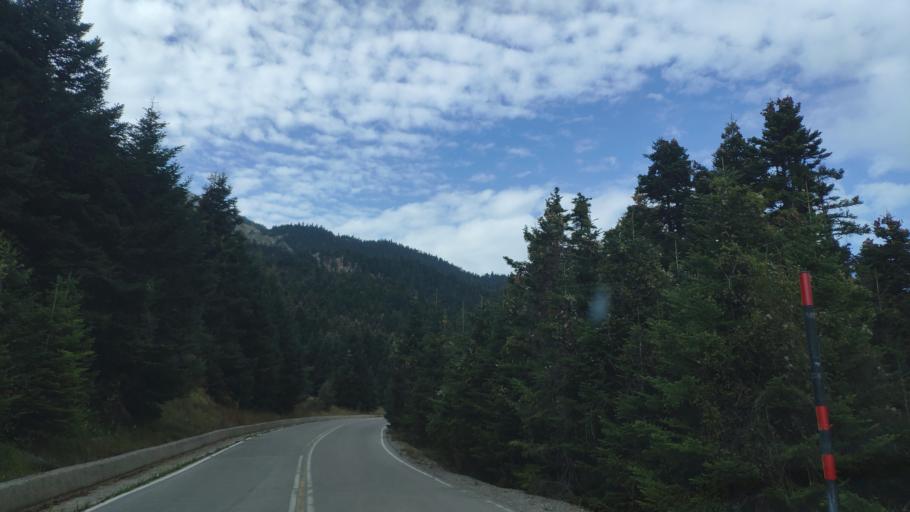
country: GR
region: Central Greece
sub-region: Nomos Fokidos
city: Amfissa
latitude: 38.6752
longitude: 22.3193
